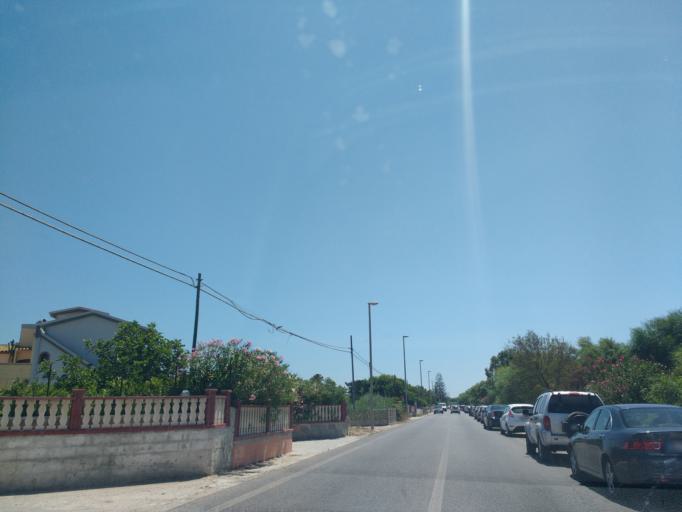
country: IT
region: Sicily
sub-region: Ragusa
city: Ispica
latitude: 36.7225
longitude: 14.9161
